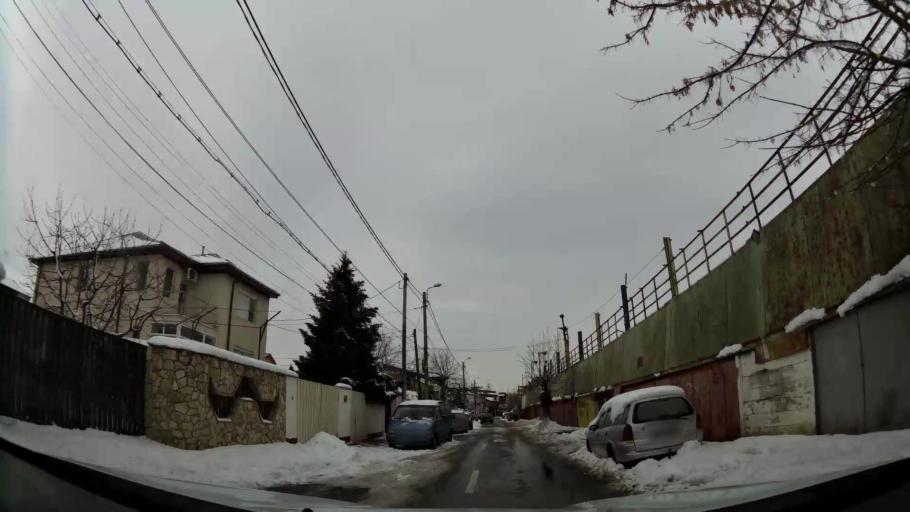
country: RO
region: Bucuresti
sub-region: Municipiul Bucuresti
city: Bucuresti
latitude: 44.3903
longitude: 26.1028
